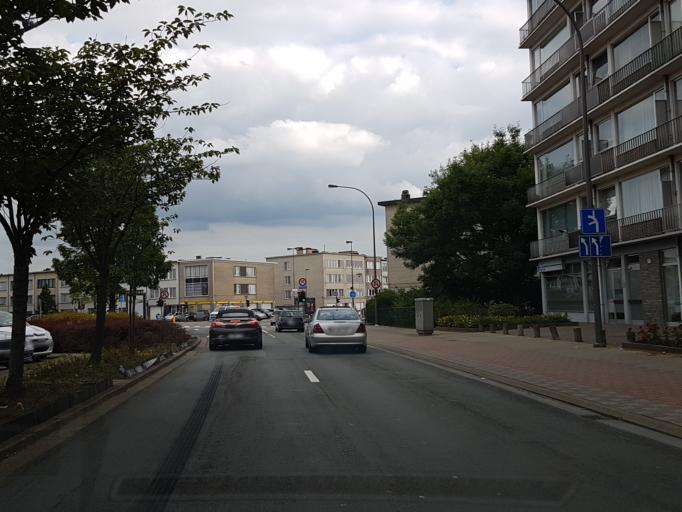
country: BE
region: Flanders
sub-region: Provincie Antwerpen
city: Antwerpen
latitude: 51.2556
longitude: 4.4348
